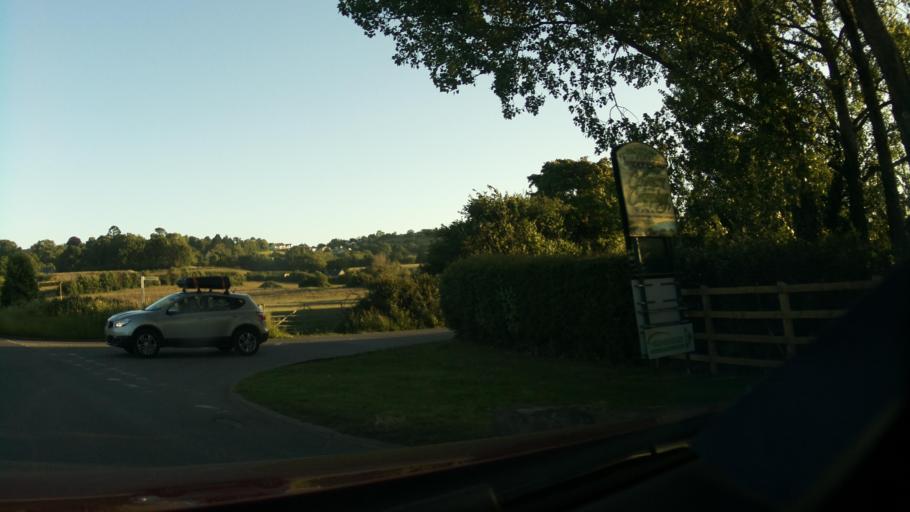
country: GB
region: England
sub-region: Devon
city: Newton Abbot
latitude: 50.5458
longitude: -3.6168
